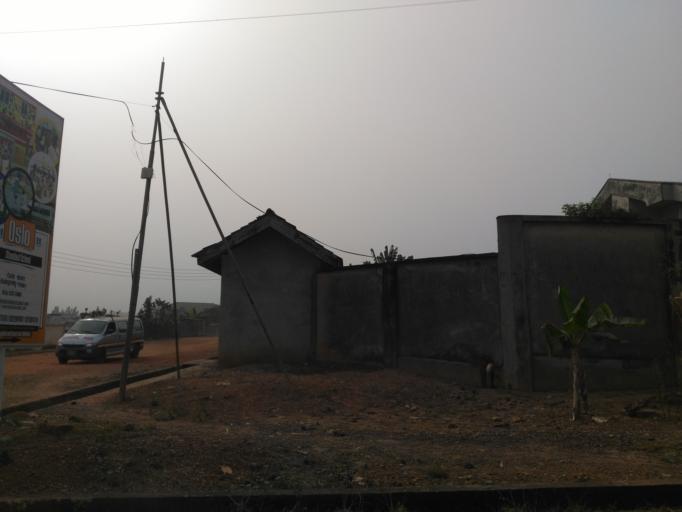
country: GH
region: Ashanti
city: Kumasi
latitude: 6.6541
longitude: -1.6266
